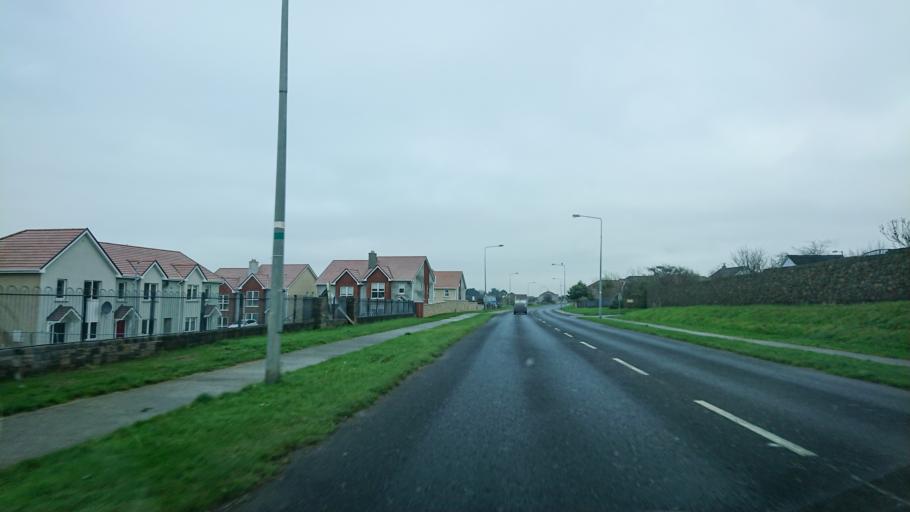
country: IE
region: Munster
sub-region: Waterford
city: Tra Mhor
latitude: 52.1677
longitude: -7.1614
